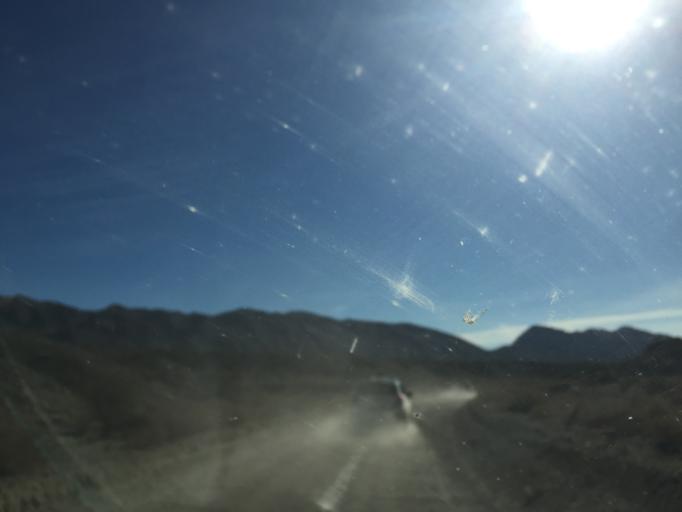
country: US
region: California
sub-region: Inyo County
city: Lone Pine
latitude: 36.7965
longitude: -117.5170
